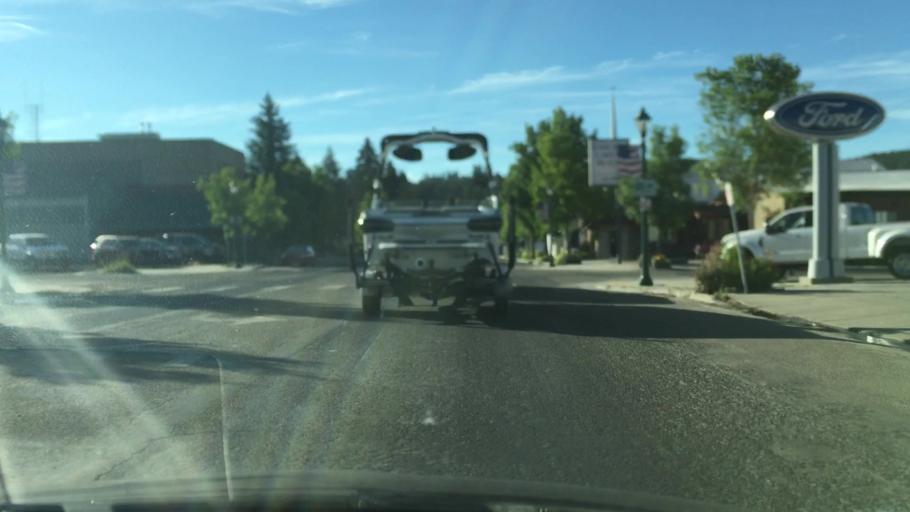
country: US
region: Idaho
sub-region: Valley County
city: Cascade
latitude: 44.5166
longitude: -116.0424
